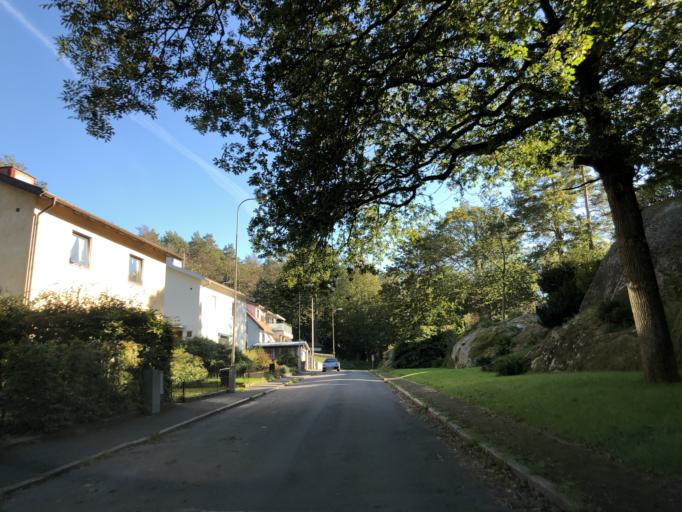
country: SE
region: Vaestra Goetaland
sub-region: Molndal
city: Moelndal
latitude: 57.6874
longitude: 12.0143
